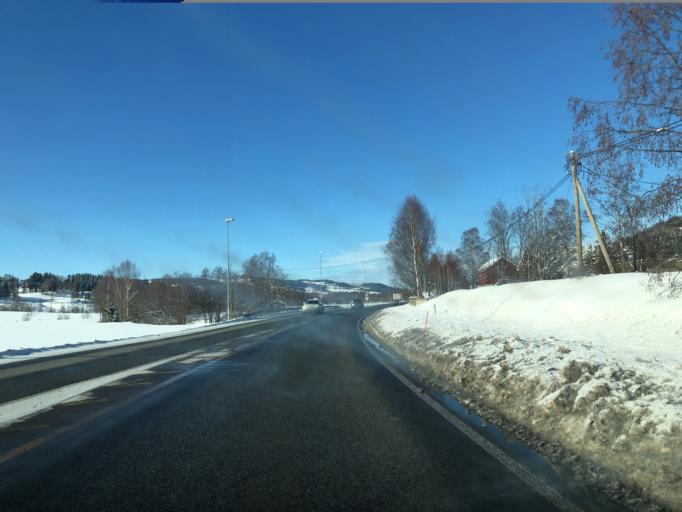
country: NO
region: Oppland
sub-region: Lunner
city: Roa
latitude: 60.2961
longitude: 10.6088
